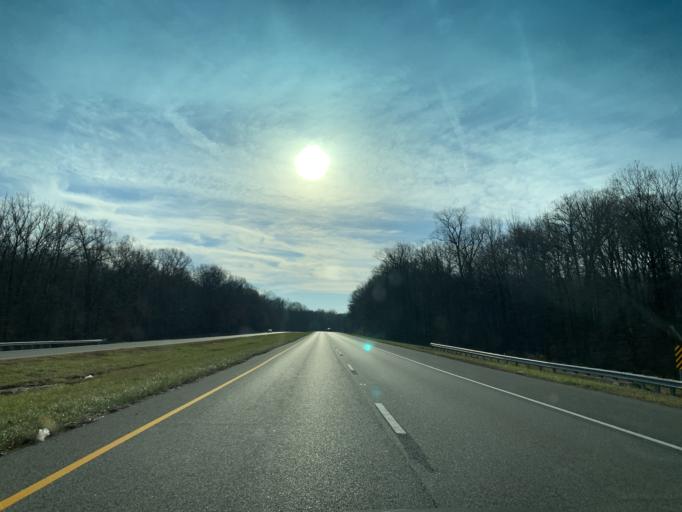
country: US
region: Maryland
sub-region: Cecil County
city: Elkton
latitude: 39.6278
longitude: -75.8147
